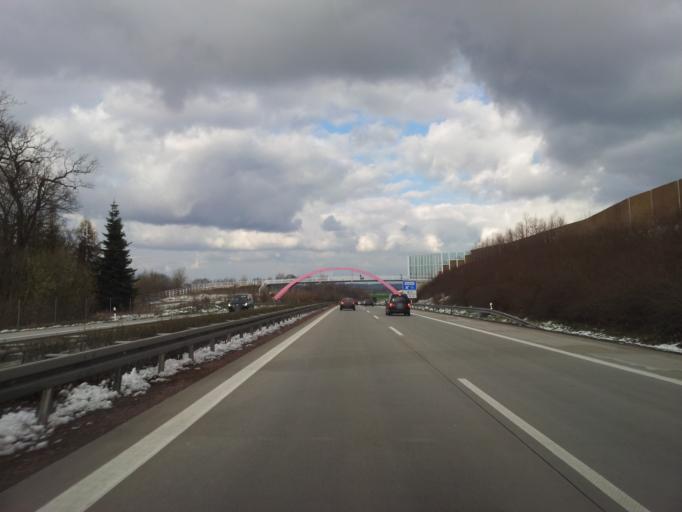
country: DE
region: Saxony
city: Stollberg
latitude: 50.7180
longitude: 12.7653
